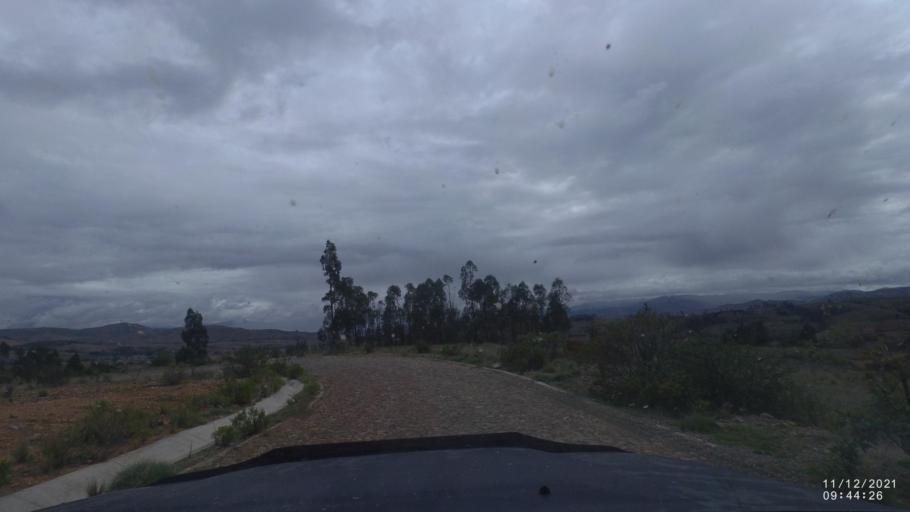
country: BO
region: Cochabamba
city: Tarata
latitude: -17.7966
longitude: -65.9728
